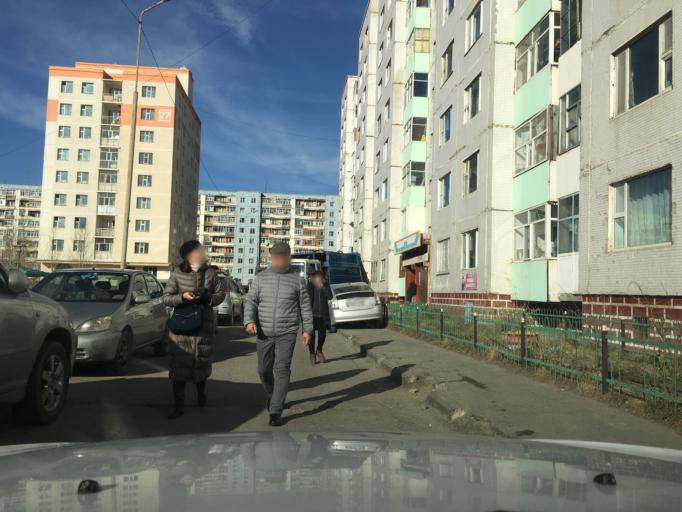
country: MN
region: Ulaanbaatar
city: Ulaanbaatar
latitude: 47.9151
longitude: 106.8451
